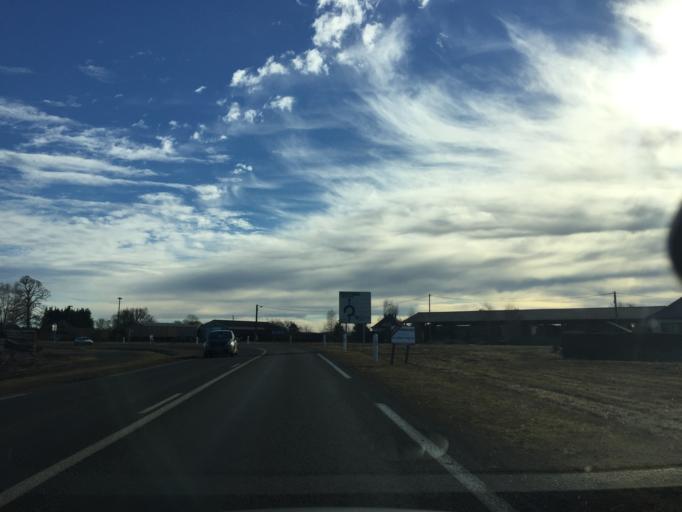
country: FR
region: Limousin
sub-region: Departement de la Creuse
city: Auzances
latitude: 45.8717
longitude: 2.5170
